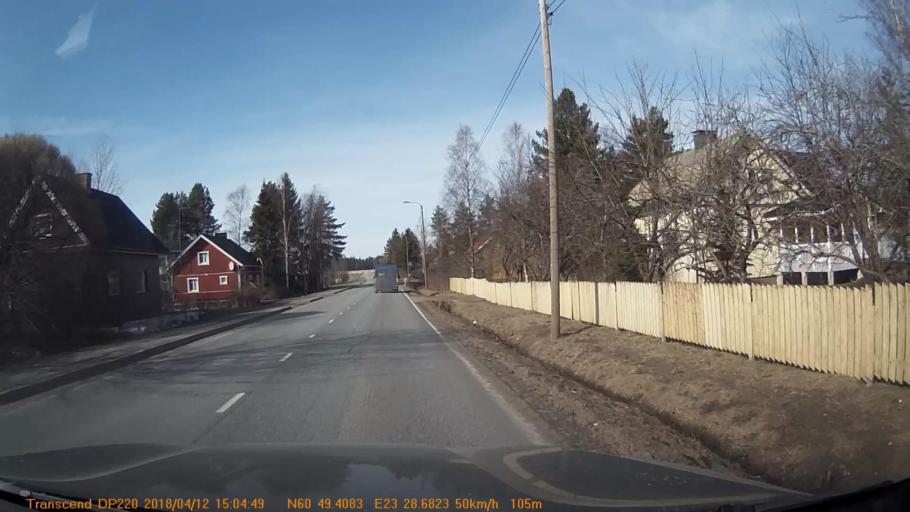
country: FI
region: Haeme
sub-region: Forssa
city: Jokioinen
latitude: 60.8237
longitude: 23.4779
